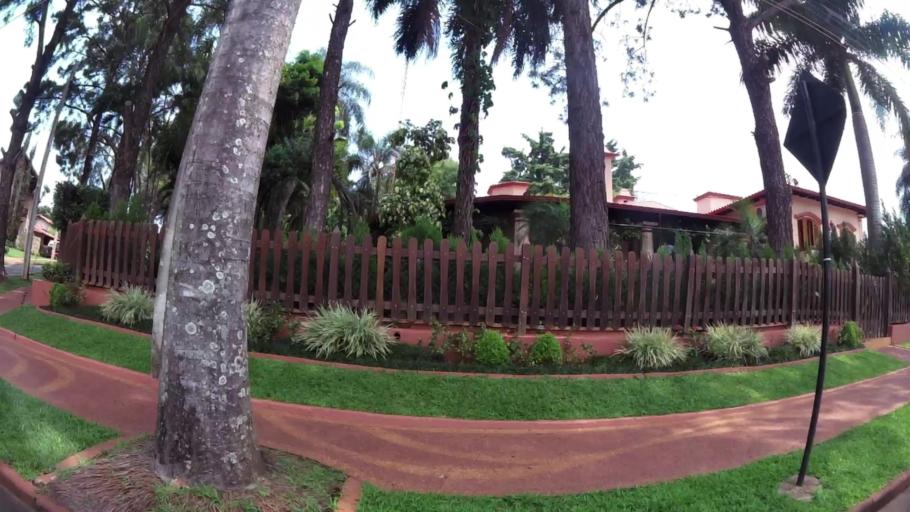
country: PY
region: Alto Parana
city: Ciudad del Este
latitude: -25.4826
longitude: -54.6186
